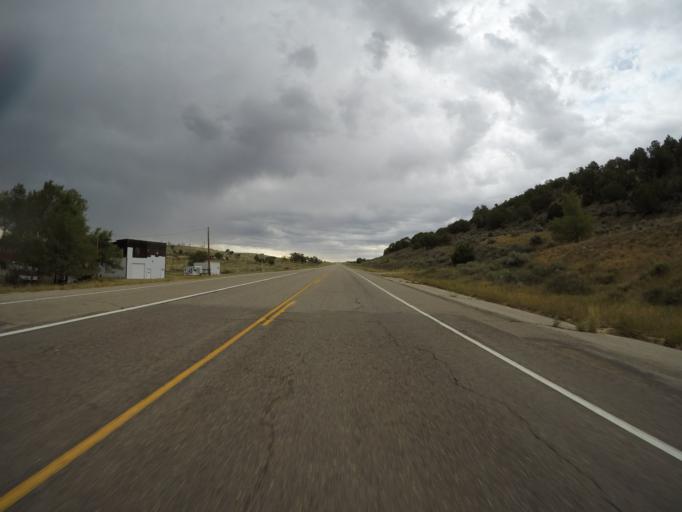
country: US
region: Colorado
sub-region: Rio Blanco County
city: Rangely
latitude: 40.3551
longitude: -108.4488
